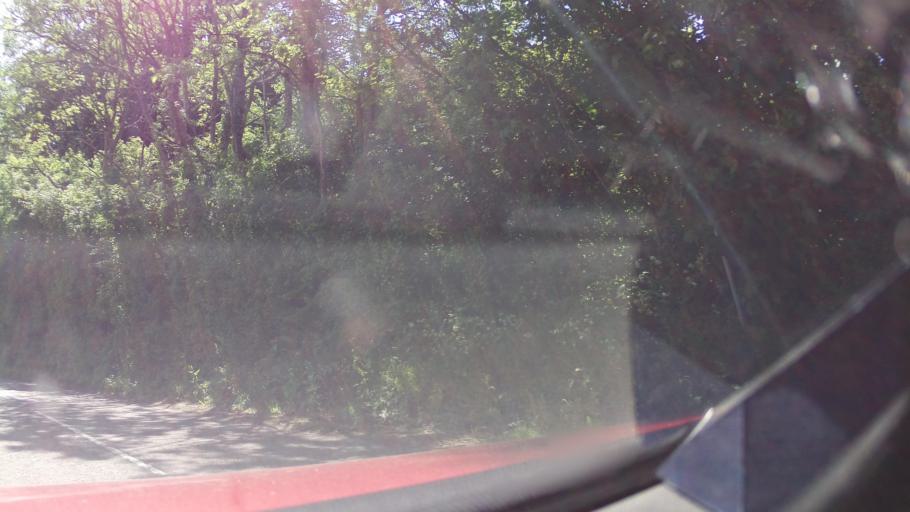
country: GB
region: England
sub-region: Devon
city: Sidmouth
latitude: 50.7043
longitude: -3.2662
